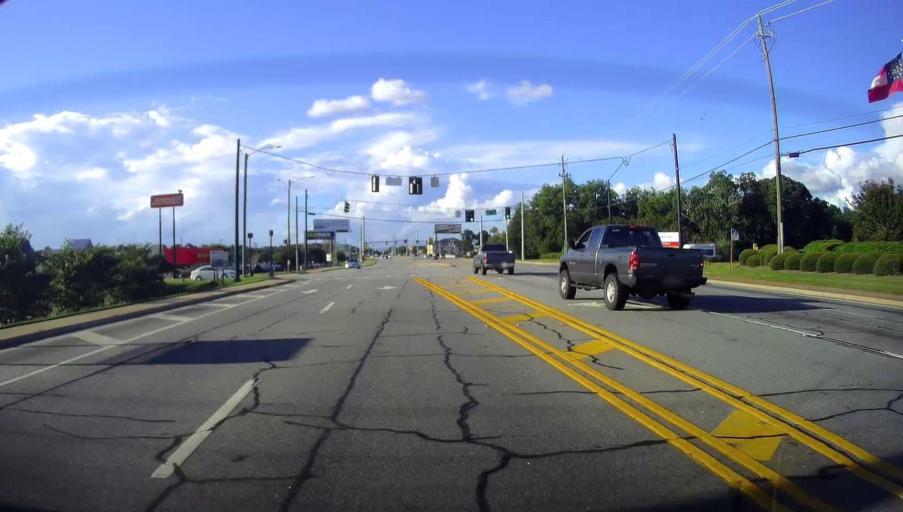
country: US
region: Alabama
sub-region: Russell County
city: Phenix City
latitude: 32.5355
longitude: -84.9549
